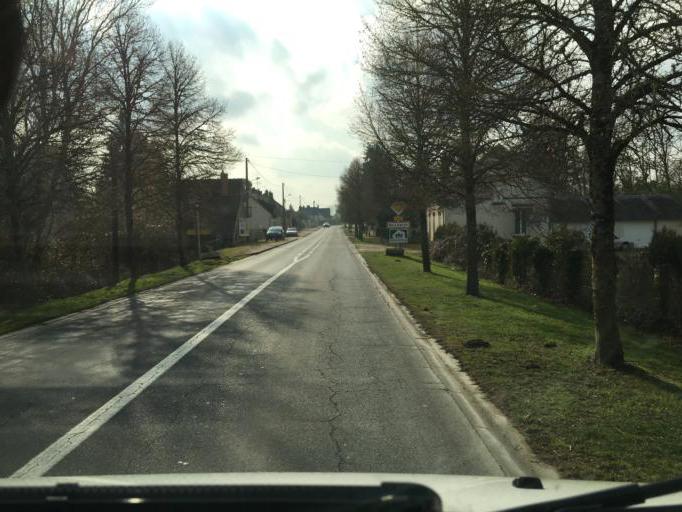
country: FR
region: Centre
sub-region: Departement du Loir-et-Cher
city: Romorantin-Lanthenay
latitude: 47.4502
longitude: 1.7763
